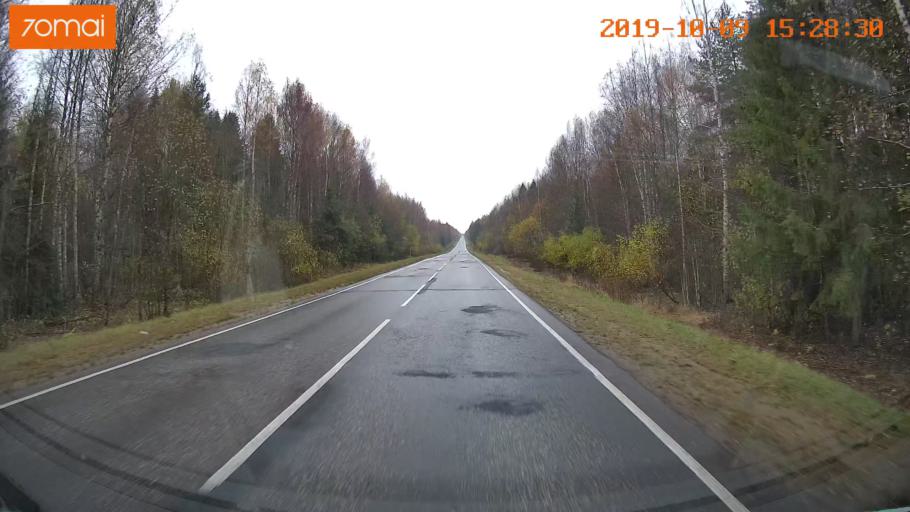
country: RU
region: Kostroma
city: Susanino
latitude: 58.0023
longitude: 41.3588
